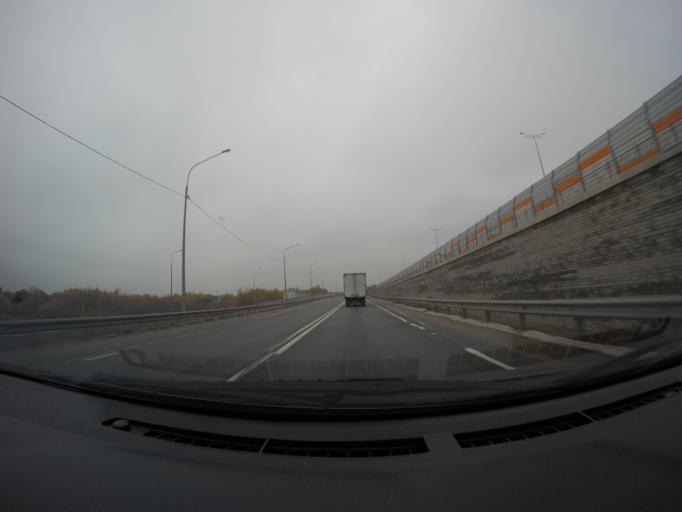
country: RU
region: Moskovskaya
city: Belyye Stolby
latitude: 55.3422
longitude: 37.8344
